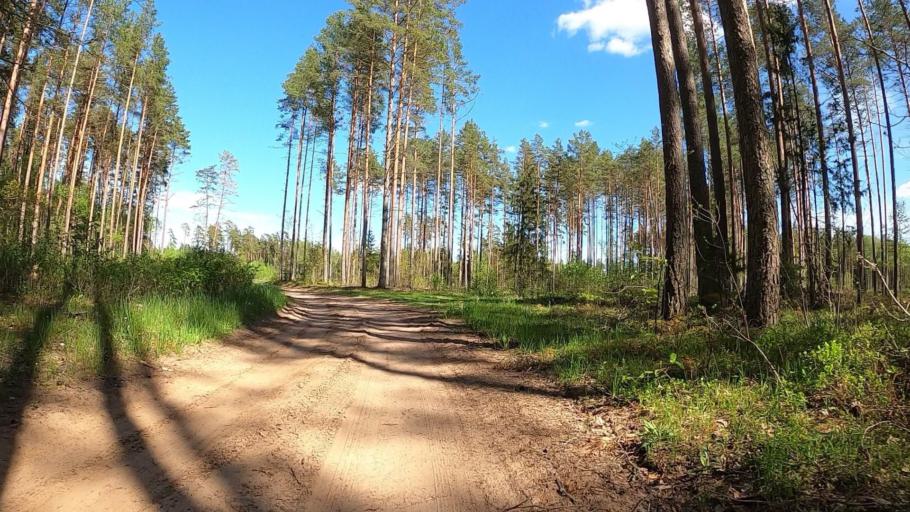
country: LV
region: Salaspils
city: Salaspils
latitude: 56.7886
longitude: 24.3242
